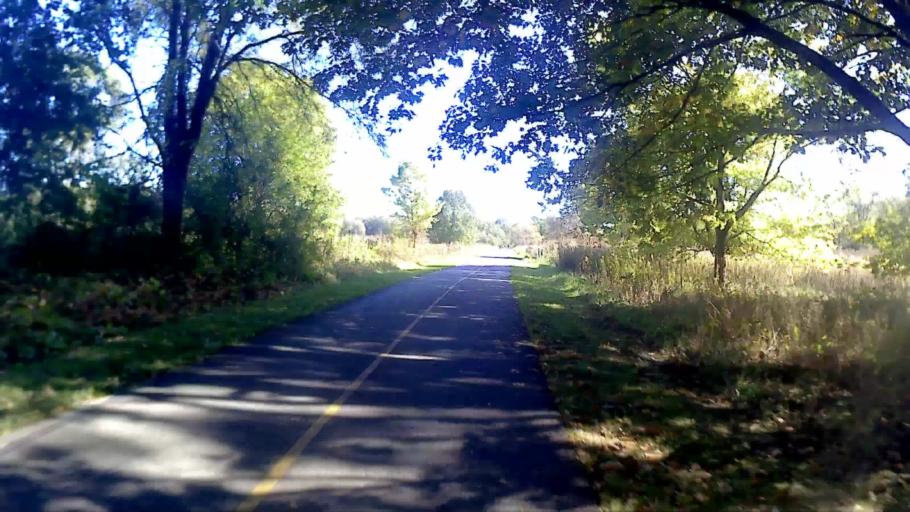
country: US
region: Illinois
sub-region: Cook County
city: Rolling Meadows
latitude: 42.0346
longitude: -88.0195
